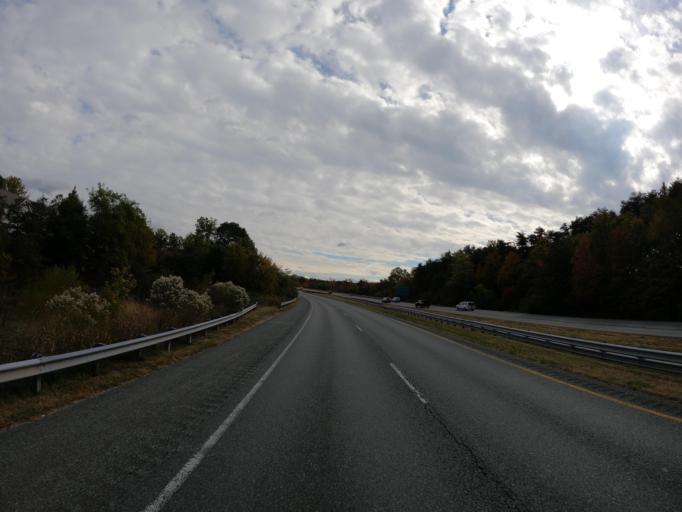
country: US
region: Maryland
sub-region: Anne Arundel County
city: Severn
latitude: 39.1491
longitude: -76.7055
